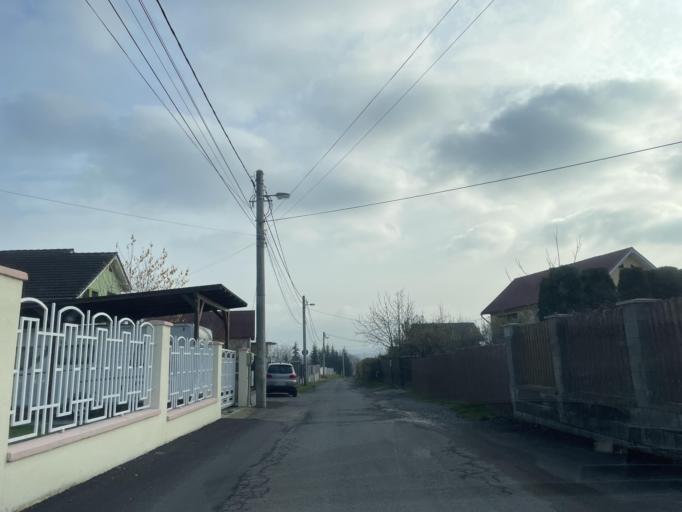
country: RO
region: Mures
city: Reghin-Sat
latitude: 46.7911
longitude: 24.7093
